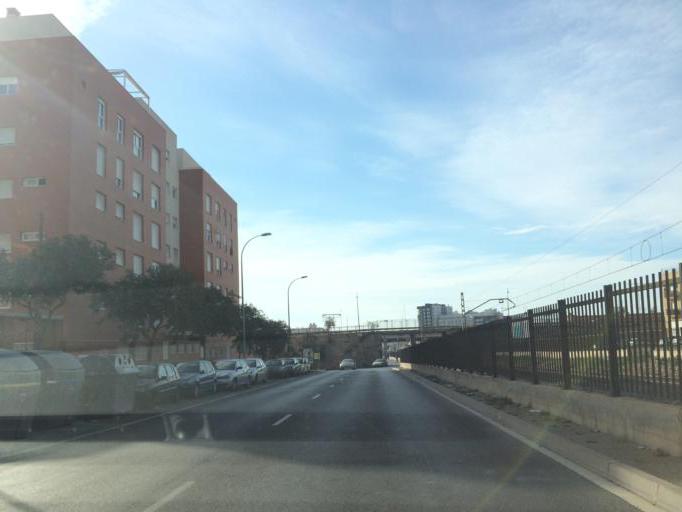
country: ES
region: Andalusia
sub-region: Provincia de Almeria
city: Almeria
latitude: 36.8453
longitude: -2.4366
